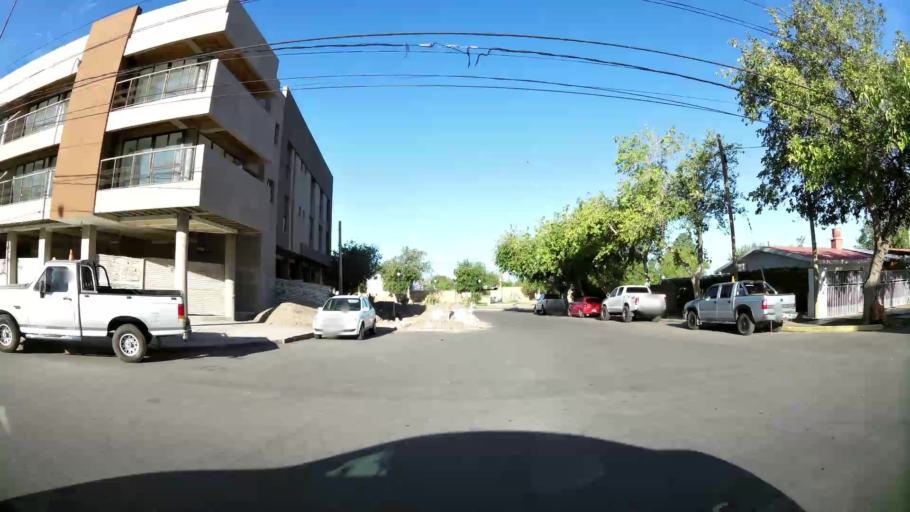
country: AR
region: San Juan
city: San Juan
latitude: -31.5481
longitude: -68.5203
